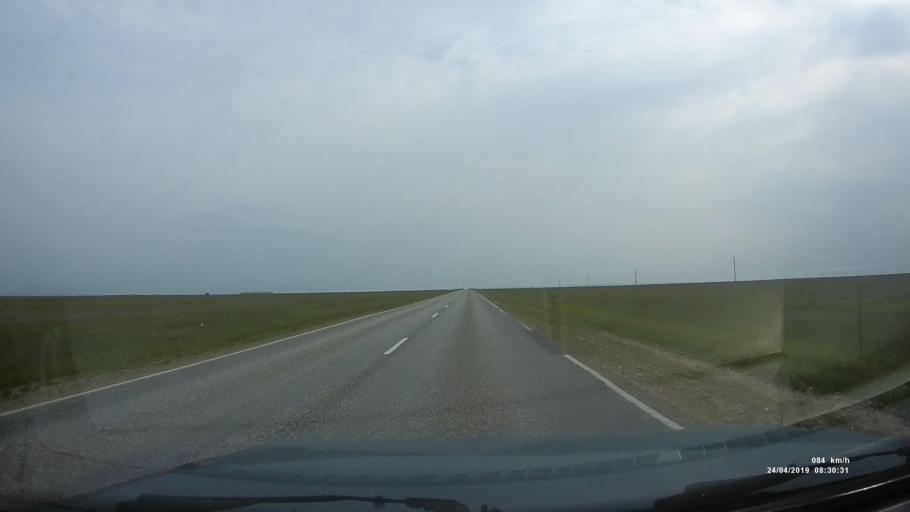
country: RU
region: Kalmykiya
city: Priyutnoye
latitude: 46.1601
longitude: 43.8466
